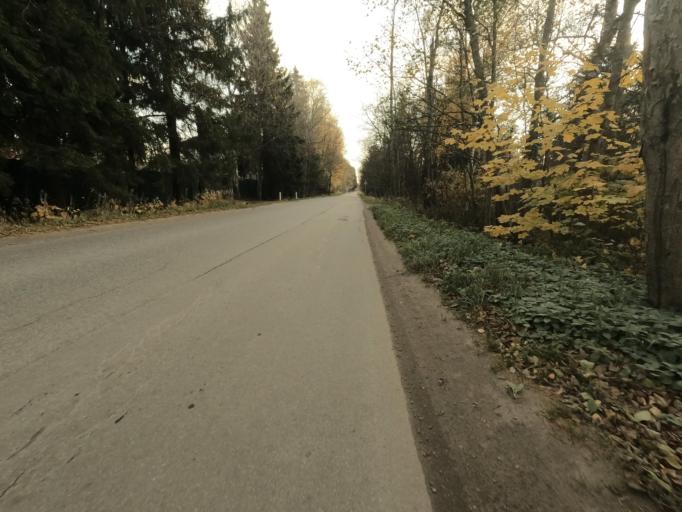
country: RU
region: St.-Petersburg
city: Beloostrov
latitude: 60.1684
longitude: 30.0116
